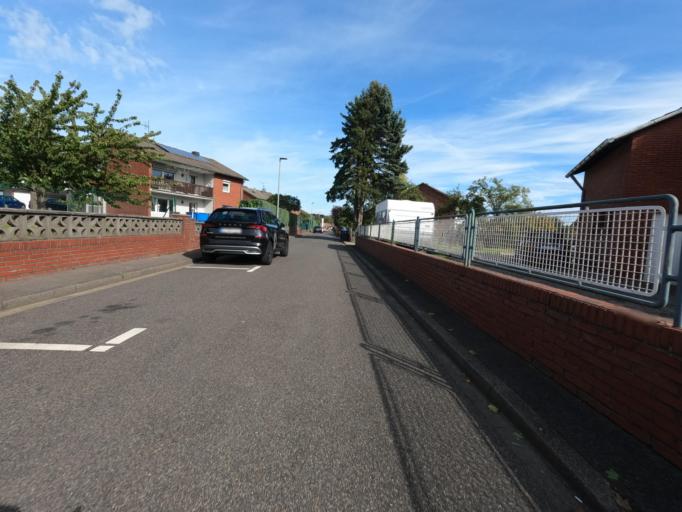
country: DE
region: North Rhine-Westphalia
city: Baesweiler
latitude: 50.9265
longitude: 6.1936
